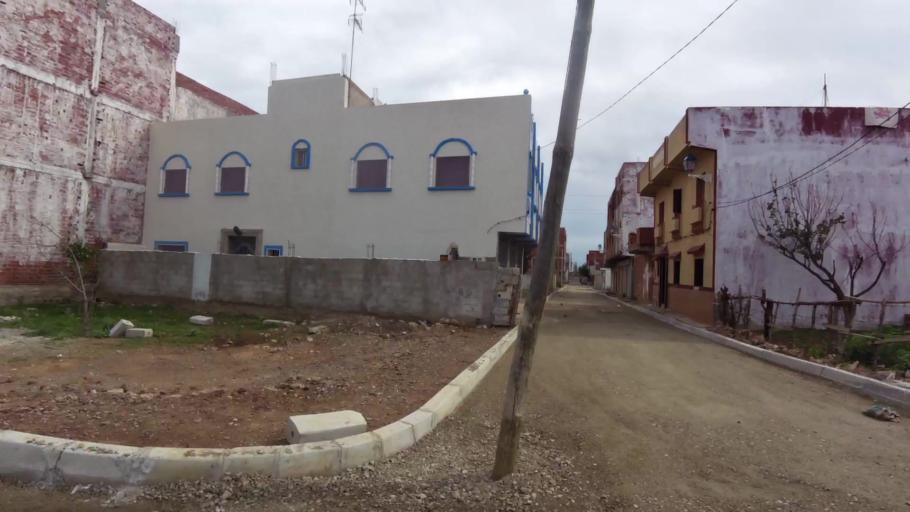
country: MA
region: Tanger-Tetouan
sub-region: Tetouan
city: Martil
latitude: 35.7021
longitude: -5.3500
